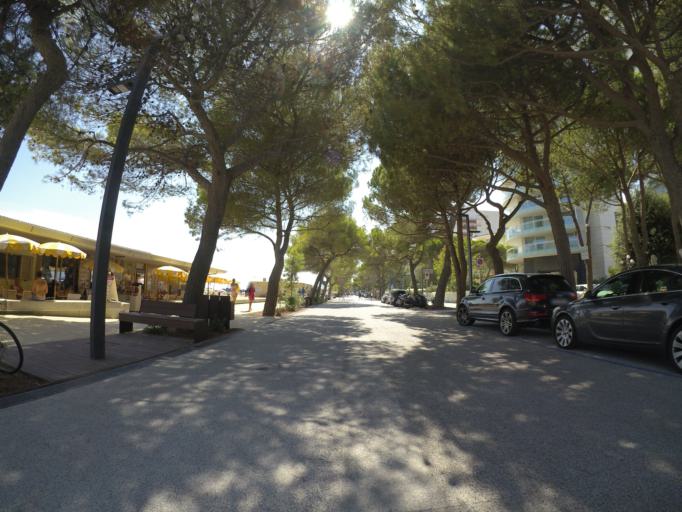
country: IT
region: Friuli Venezia Giulia
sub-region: Provincia di Udine
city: Lignano Sabbiadoro
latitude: 45.6814
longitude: 13.1329
